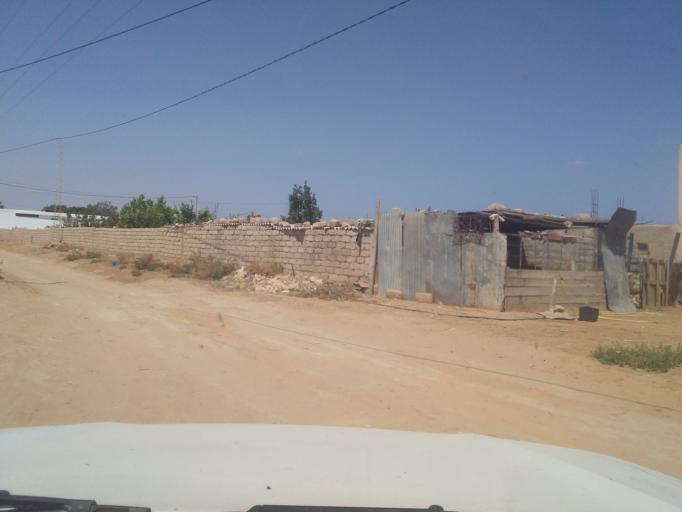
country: TN
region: Qabis
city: Matmata
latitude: 33.5936
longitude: 10.2857
